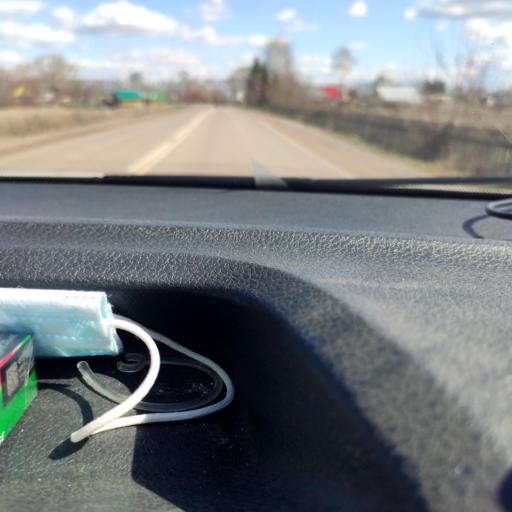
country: RU
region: Bashkortostan
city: Alekseyevka
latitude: 54.7336
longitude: 55.1785
